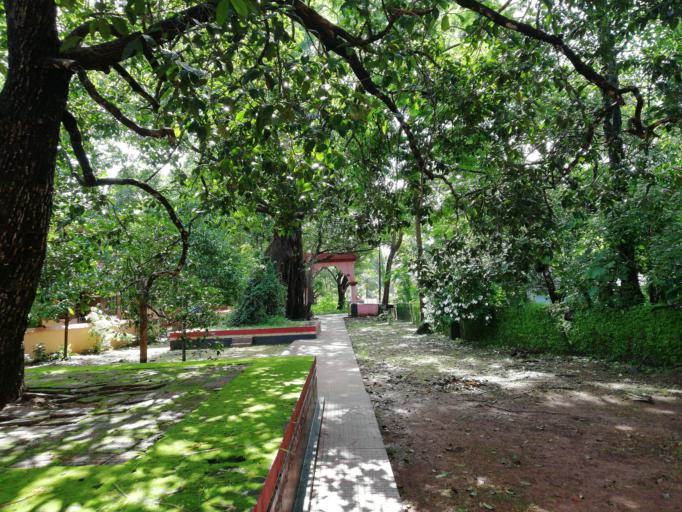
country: IN
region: Kerala
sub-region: Kannur
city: Payyannur
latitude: 12.0563
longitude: 75.1896
